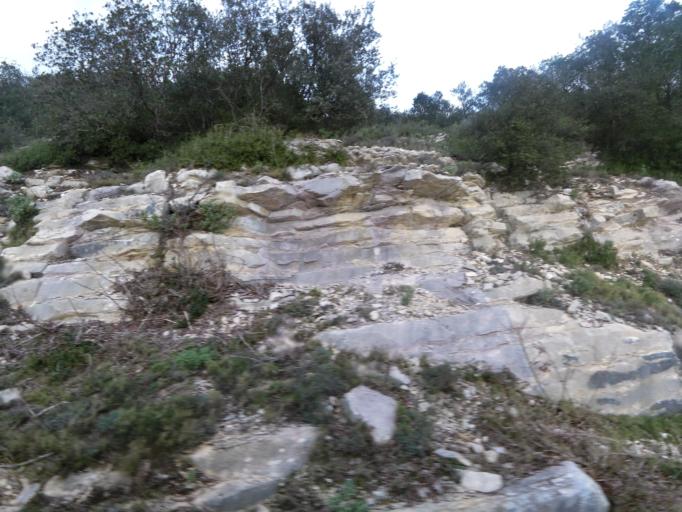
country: FR
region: Languedoc-Roussillon
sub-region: Departement du Gard
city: Clarensac
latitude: 43.8349
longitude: 4.1883
